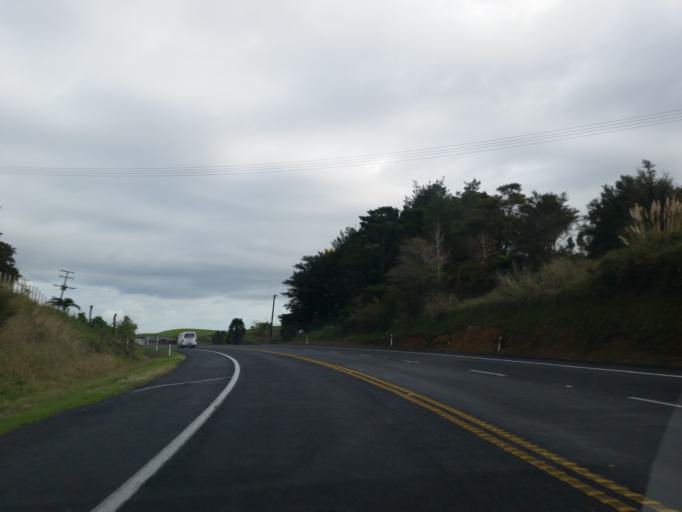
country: NZ
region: Waikato
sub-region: Hauraki District
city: Paeroa
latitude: -37.4022
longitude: 175.7062
